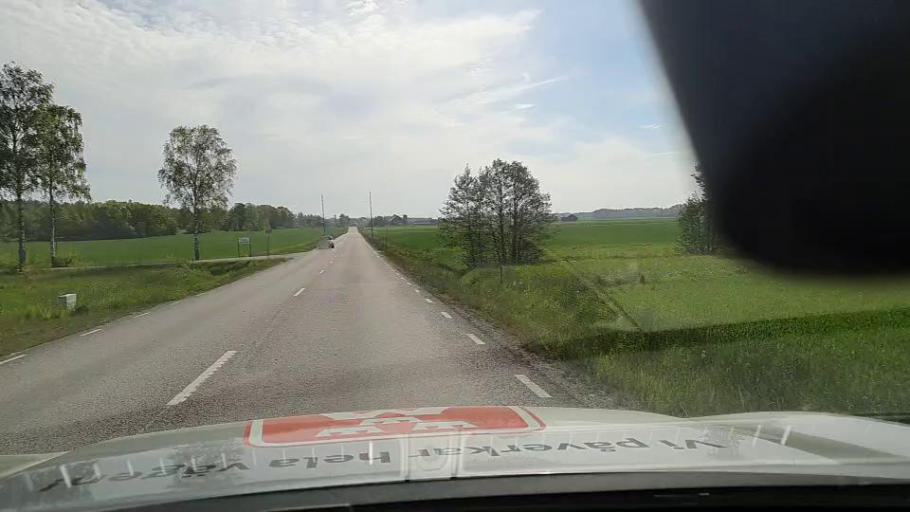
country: SE
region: Soedermanland
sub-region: Eskilstuna Kommun
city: Skogstorp
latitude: 59.3179
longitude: 16.5378
